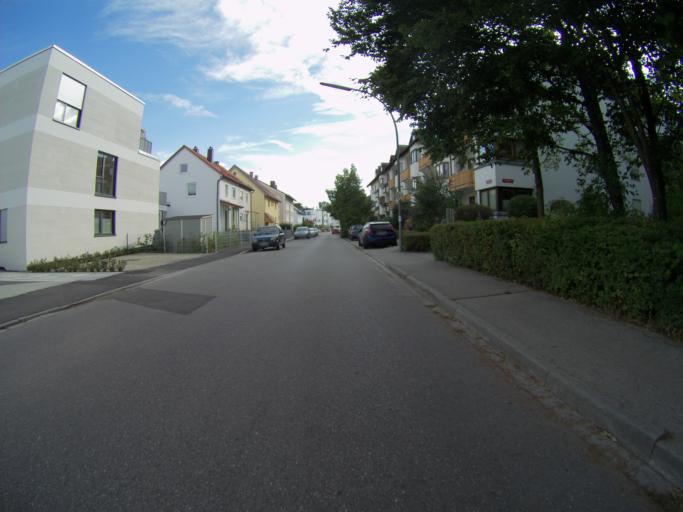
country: DE
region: Bavaria
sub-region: Upper Bavaria
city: Freising
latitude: 48.3933
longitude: 11.7386
